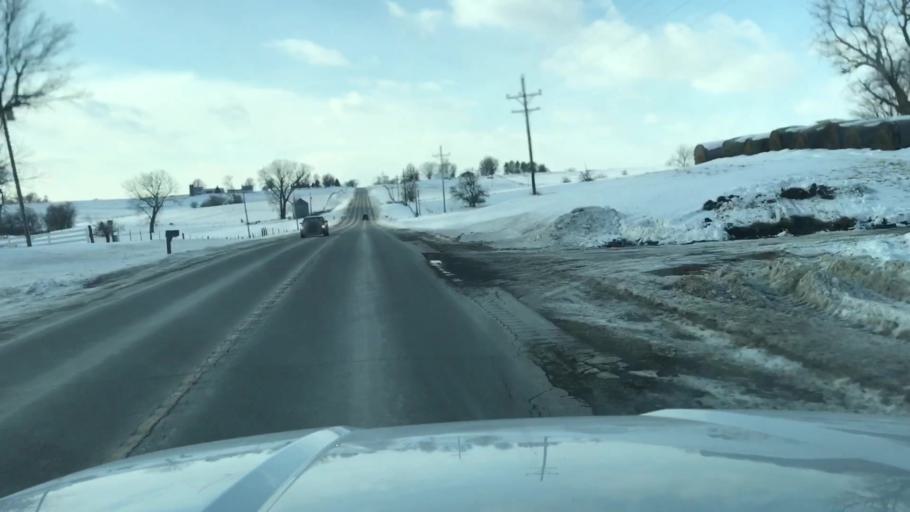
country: US
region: Missouri
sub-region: Nodaway County
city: Maryville
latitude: 40.3437
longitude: -94.7056
